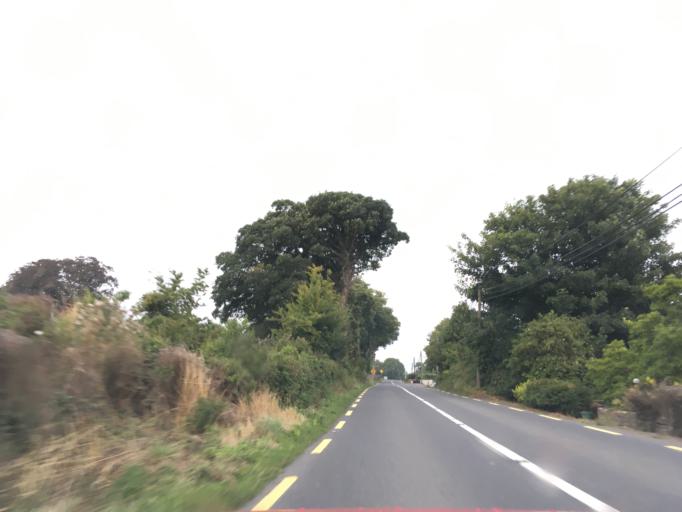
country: IE
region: Munster
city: Cashel
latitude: 52.4959
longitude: -7.9978
